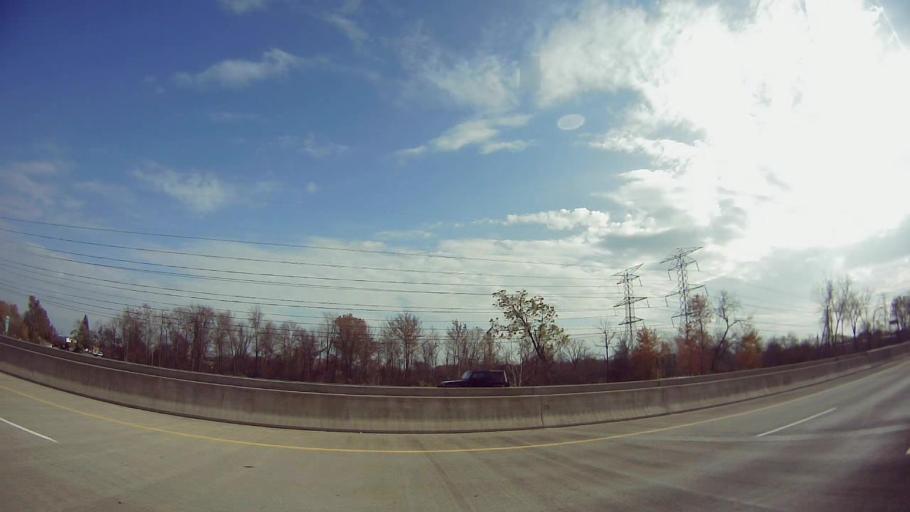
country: US
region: Michigan
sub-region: Monroe County
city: South Rockwood
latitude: 42.0680
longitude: -83.2543
